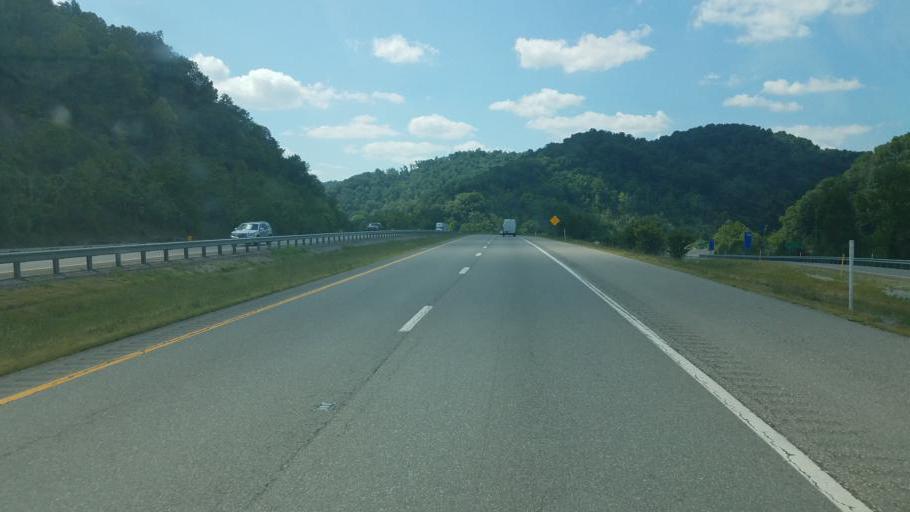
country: US
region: West Virginia
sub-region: Kanawha County
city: Charleston
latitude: 38.4112
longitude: -81.6264
